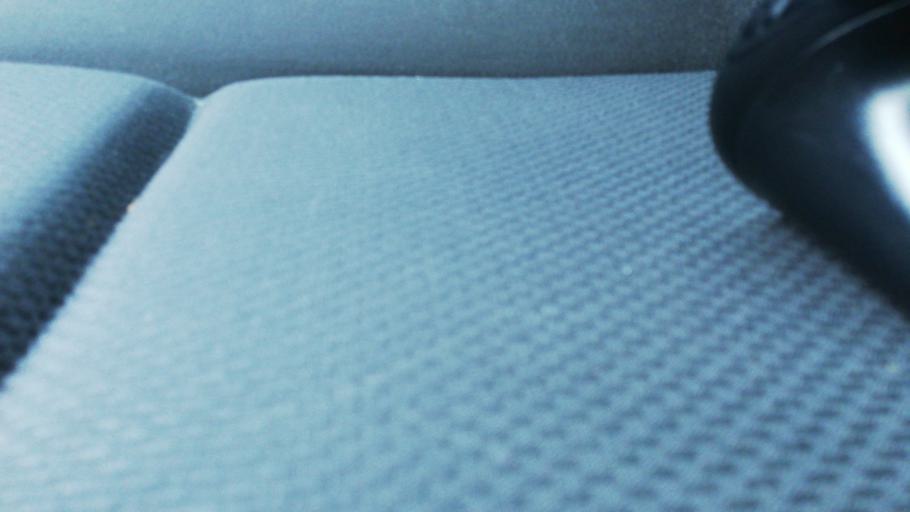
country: SK
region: Nitriansky
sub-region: Okres Nitra
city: Nitra
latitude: 48.3199
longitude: 17.9877
